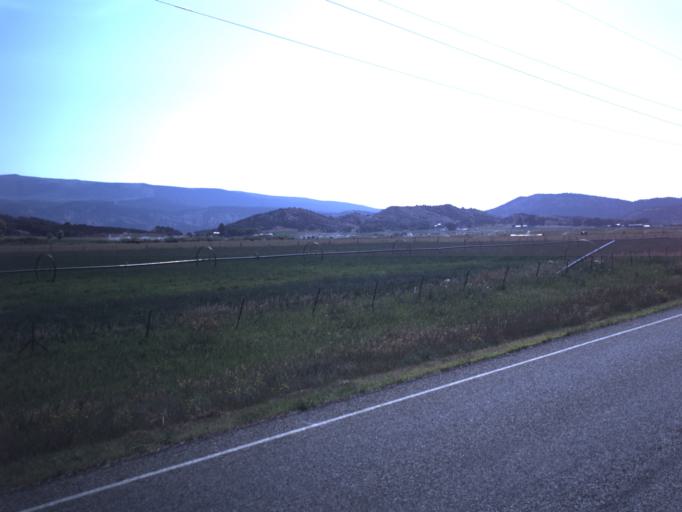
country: US
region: Utah
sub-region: Duchesne County
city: Duchesne
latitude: 40.3790
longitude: -110.7359
